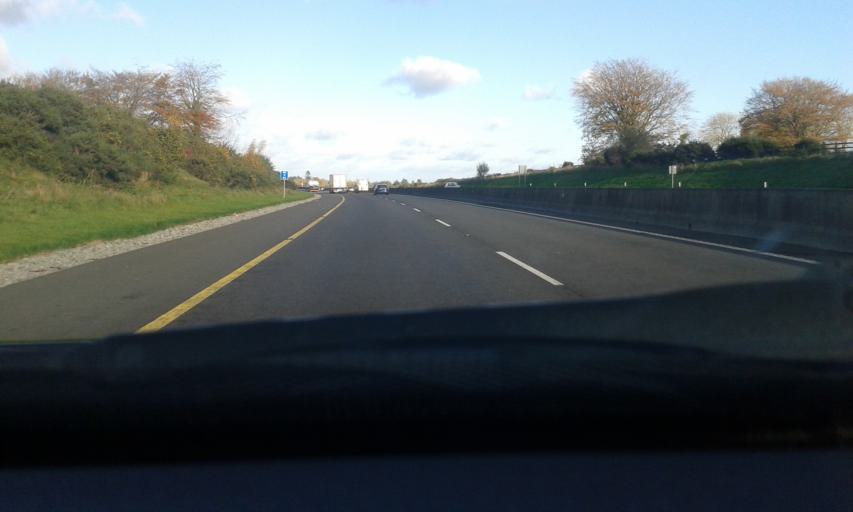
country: IE
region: Munster
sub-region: County Cork
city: Mitchelstown
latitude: 52.2981
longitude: -8.1807
